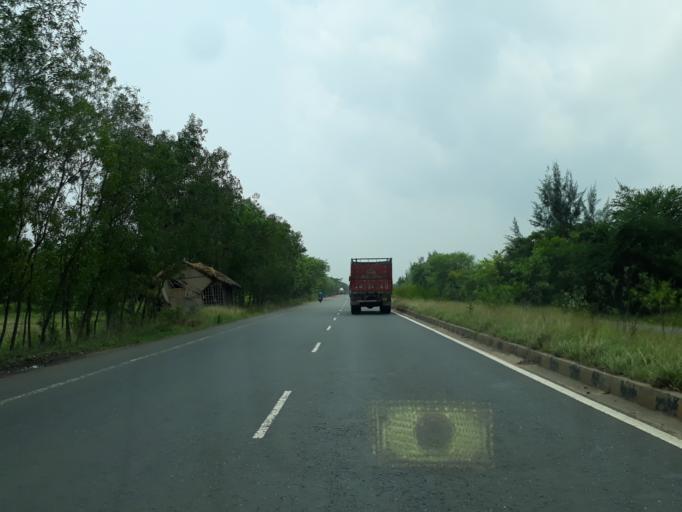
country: IN
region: West Bengal
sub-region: Purba Medinipur
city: Mahishadal
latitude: 22.1307
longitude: 87.9929
